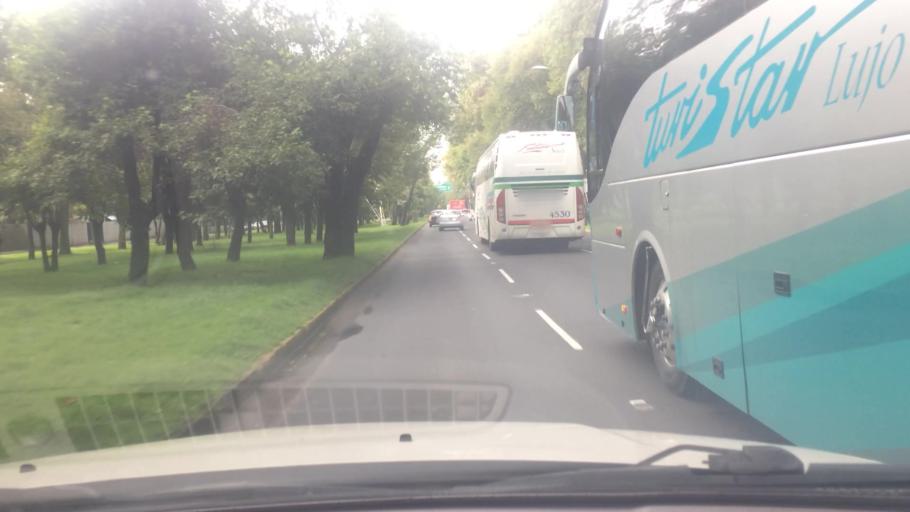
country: MX
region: Mexico City
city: Colonia Nativitas
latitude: 19.3519
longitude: -99.1303
